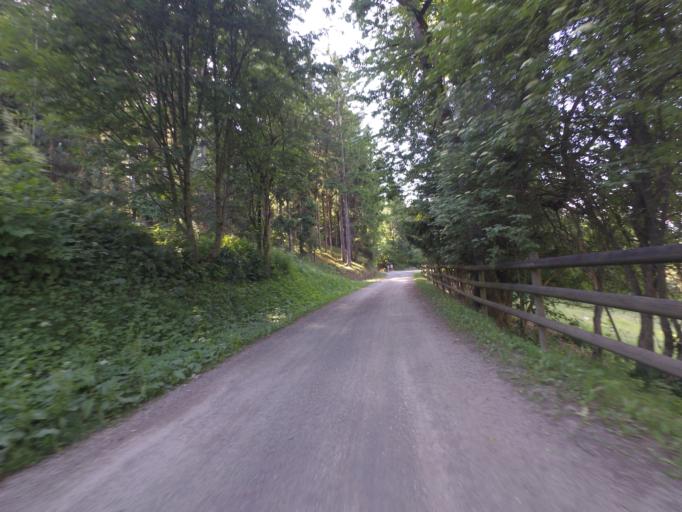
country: AT
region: Carinthia
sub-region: Politischer Bezirk Spittal an der Drau
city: Seeboden
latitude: 46.8072
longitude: 13.5242
